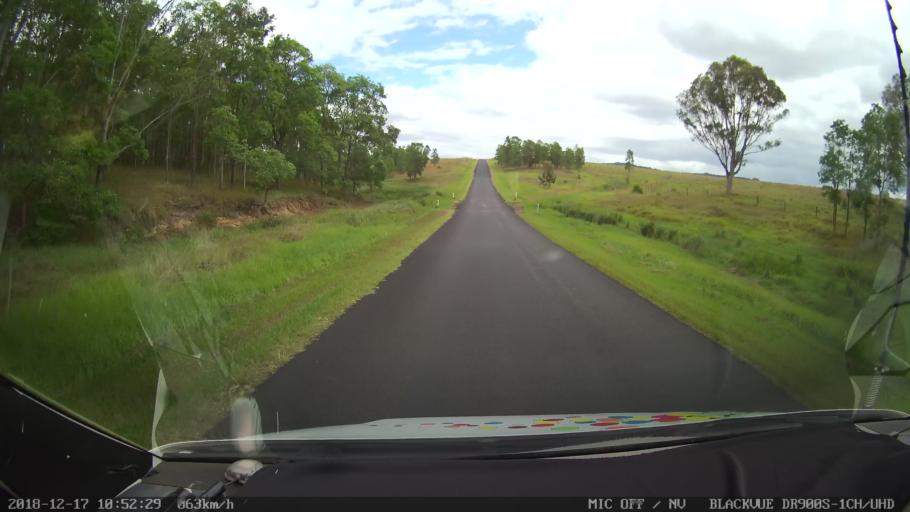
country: AU
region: New South Wales
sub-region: Tenterfield Municipality
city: Carrolls Creek
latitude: -28.8449
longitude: 152.5634
